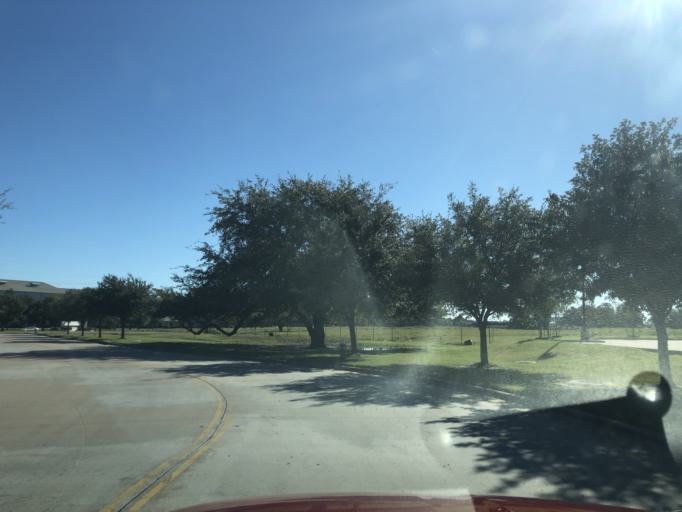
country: US
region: Texas
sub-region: Harris County
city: Oak Cliff Place
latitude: 29.9342
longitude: -95.6517
